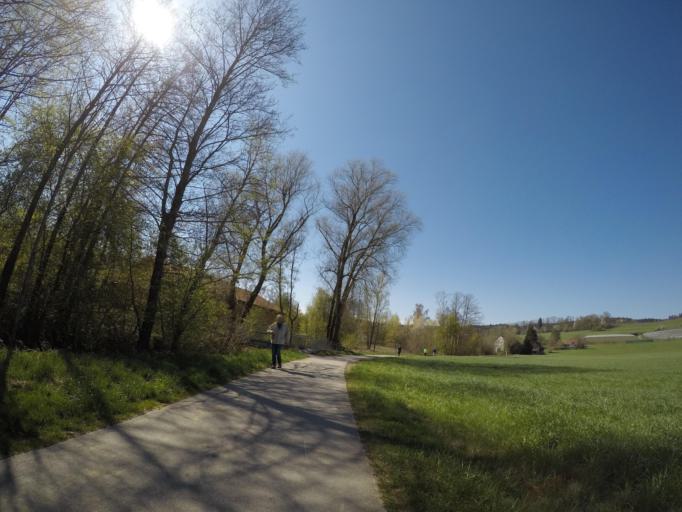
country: DE
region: Baden-Wuerttemberg
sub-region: Tuebingen Region
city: Horgenzell
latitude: 47.8256
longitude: 9.4584
